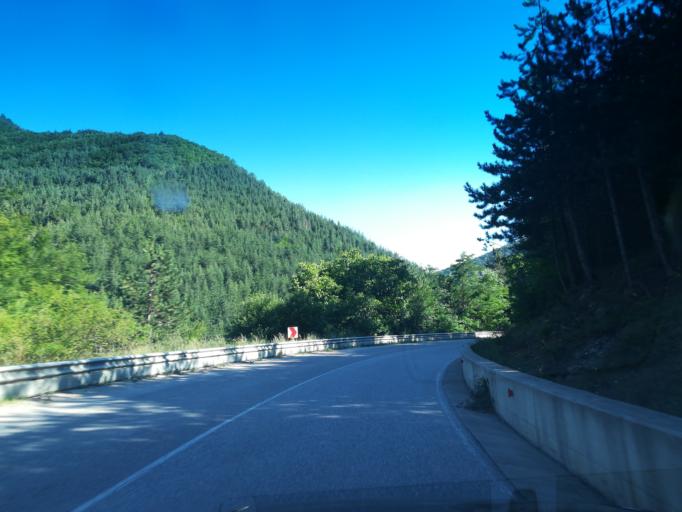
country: BG
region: Smolyan
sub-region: Obshtina Chepelare
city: Chepelare
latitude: 41.8449
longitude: 24.6813
